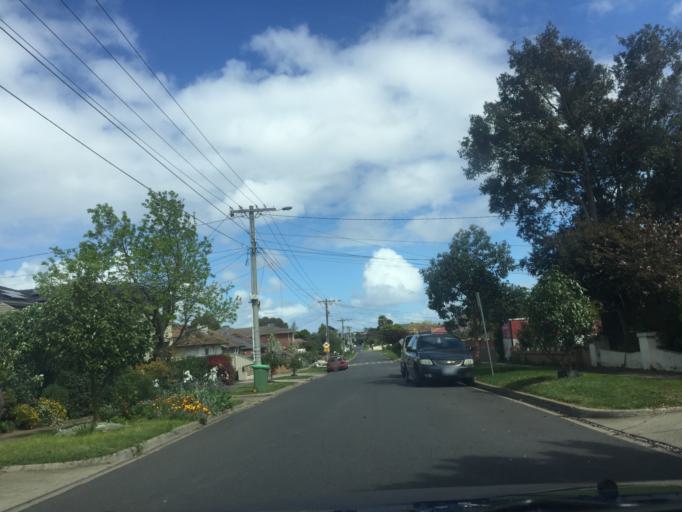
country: AU
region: Victoria
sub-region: Darebin
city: Preston
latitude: -37.7425
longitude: 145.0165
